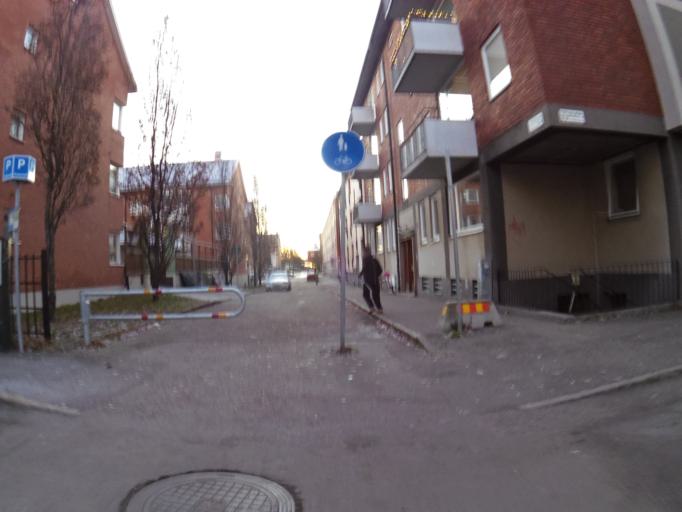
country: SE
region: Gaevleborg
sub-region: Gavle Kommun
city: Gavle
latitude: 60.6682
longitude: 17.1482
